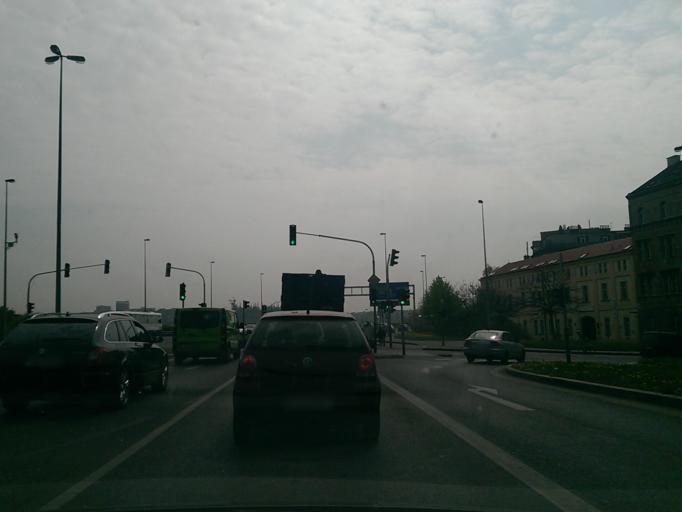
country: CZ
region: Praha
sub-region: Praha 2
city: Vysehrad
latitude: 50.0633
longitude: 14.4050
